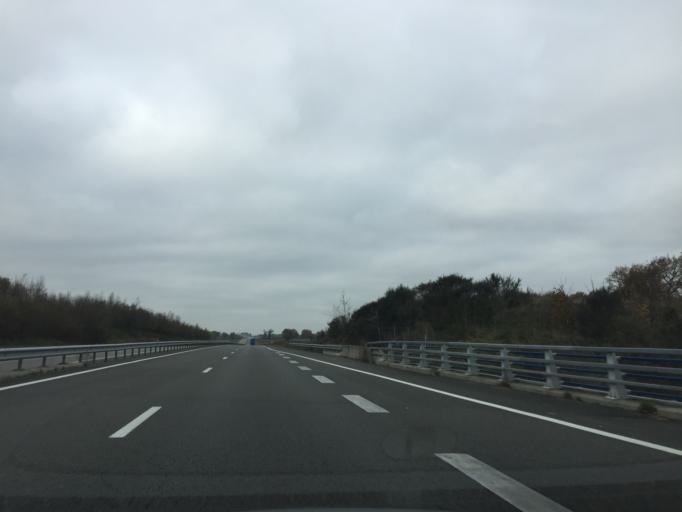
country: FR
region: Limousin
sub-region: Departement de la Creuse
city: Chambon-sur-Voueize
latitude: 46.2789
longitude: 2.3929
